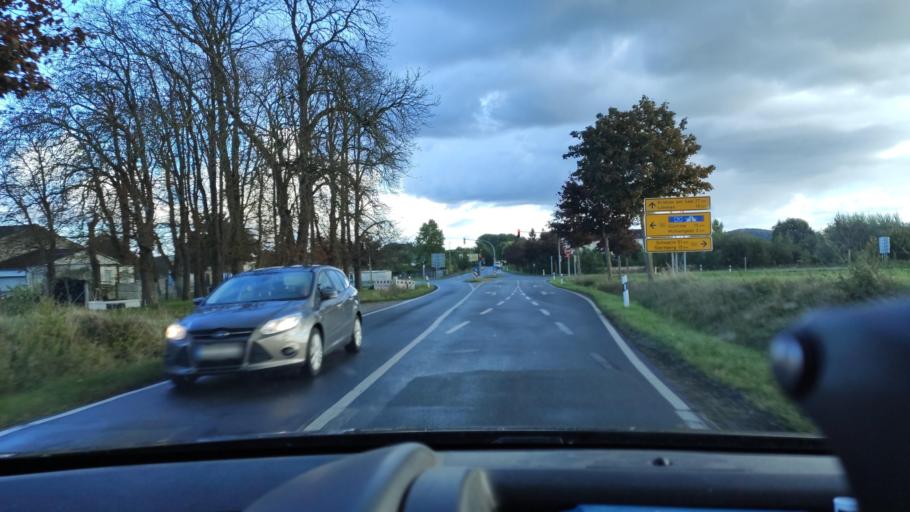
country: DE
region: Mecklenburg-Vorpommern
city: Tarnow
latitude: 53.7550
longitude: 12.0333
